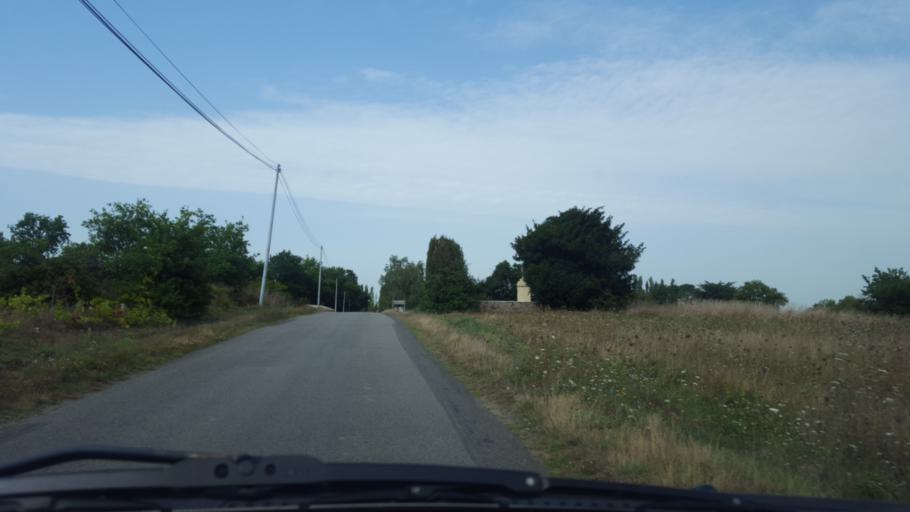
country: FR
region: Pays de la Loire
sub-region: Departement de la Loire-Atlantique
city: Saint-Philbert-de-Grand-Lieu
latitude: 47.0045
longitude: -1.6325
